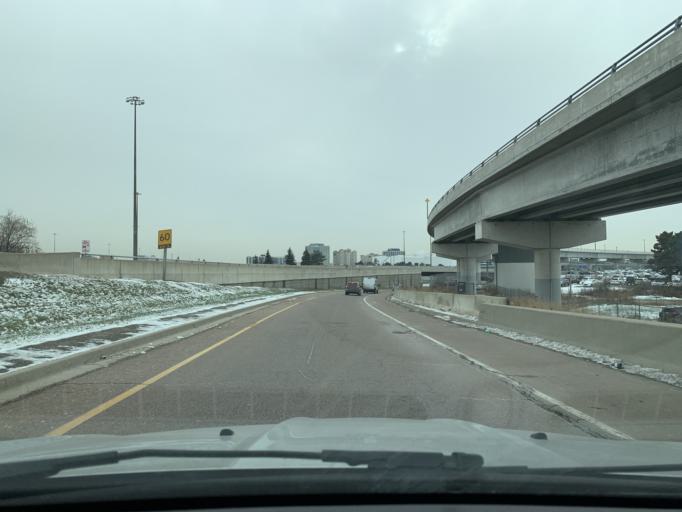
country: CA
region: Ontario
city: Etobicoke
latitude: 43.6985
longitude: -79.6099
